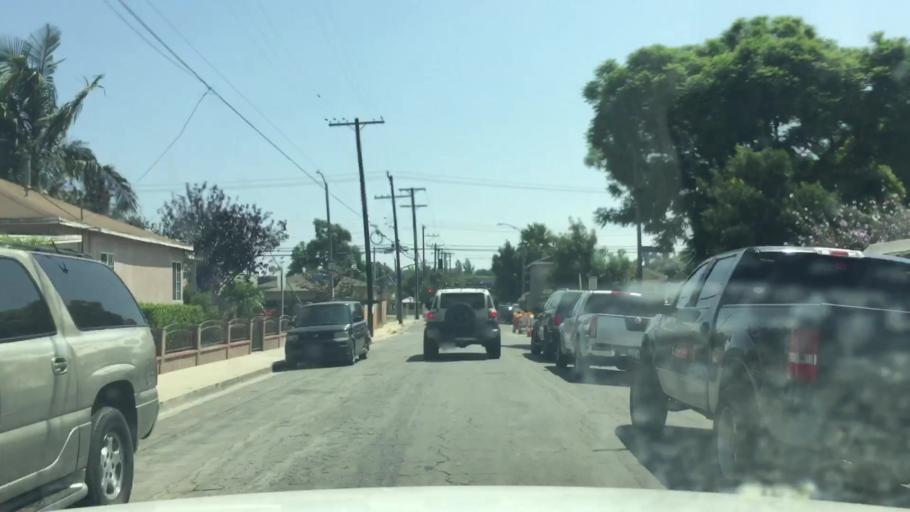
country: US
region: California
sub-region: Los Angeles County
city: Signal Hill
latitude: 33.8477
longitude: -118.1898
